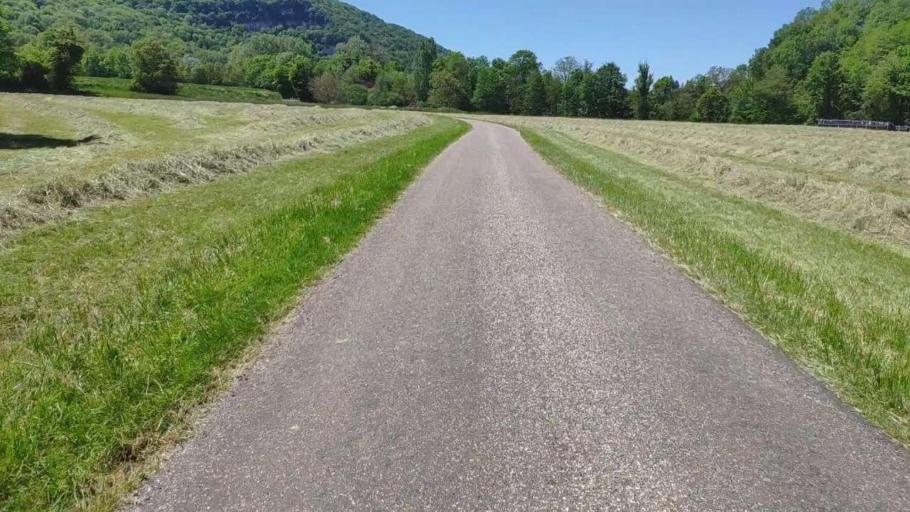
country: FR
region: Franche-Comte
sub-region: Departement du Jura
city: Perrigny
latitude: 46.7355
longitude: 5.6384
